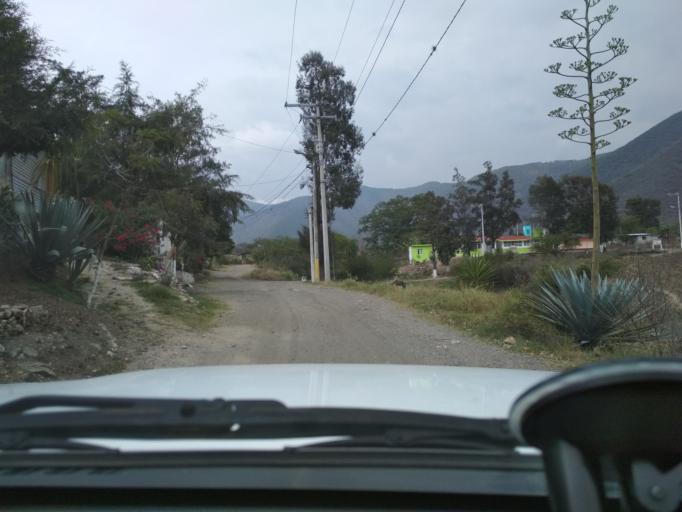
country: MX
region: Veracruz
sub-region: Nogales
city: Taza de Agua Ojo Zarco
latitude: 18.7873
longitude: -97.2100
